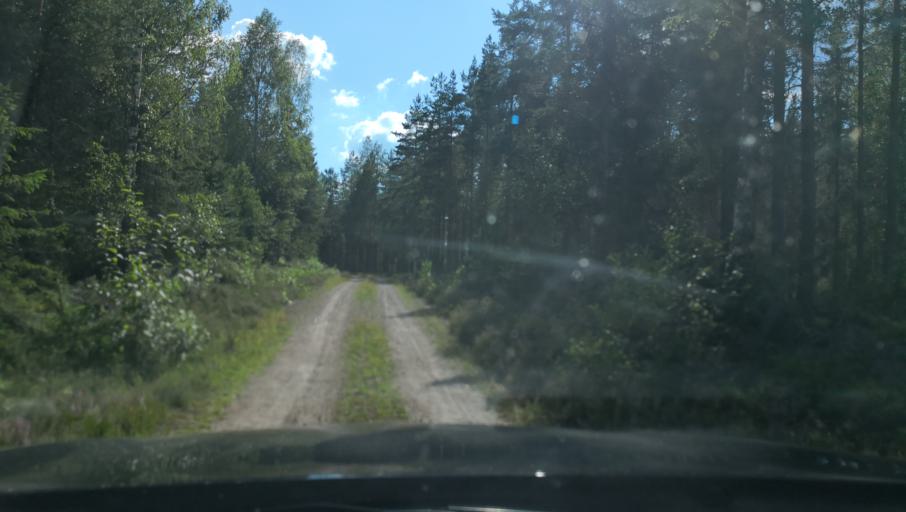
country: SE
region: Vaestmanland
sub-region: Vasteras
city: Skultuna
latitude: 59.7151
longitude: 16.3738
